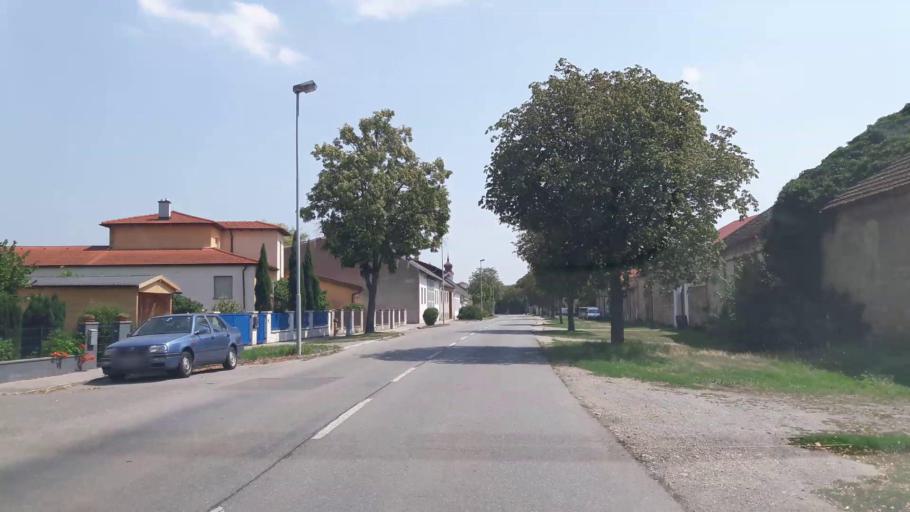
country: AT
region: Lower Austria
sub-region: Politischer Bezirk Bruck an der Leitha
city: Trautmannsdorf an der Leitha
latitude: 48.0234
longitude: 16.6348
